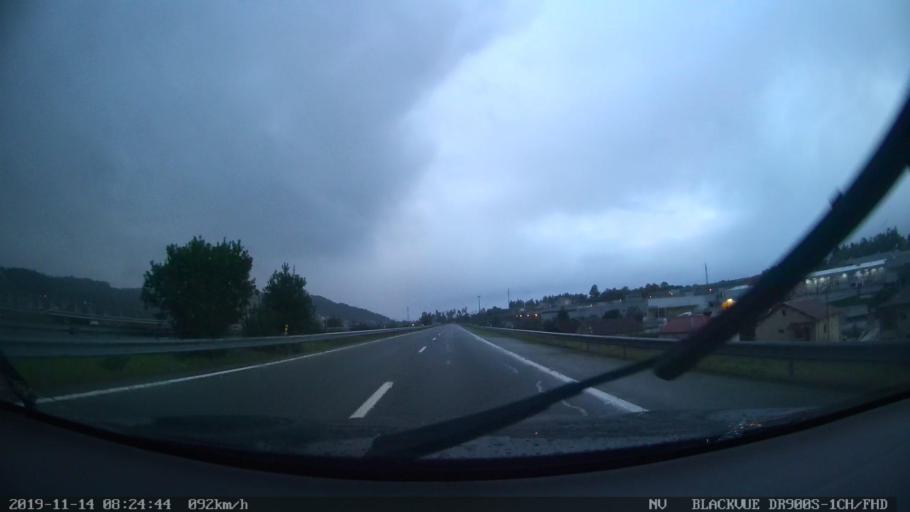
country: PT
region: Braga
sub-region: Braga
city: Oliveira
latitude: 41.5305
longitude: -8.4747
